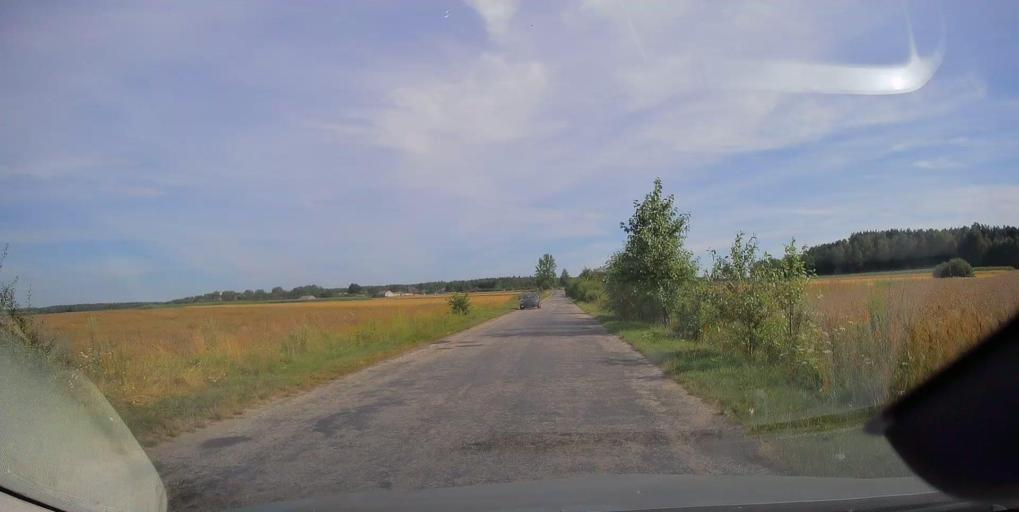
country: PL
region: Lodz Voivodeship
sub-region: Powiat opoczynski
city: Mniszkow
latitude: 51.4153
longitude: 20.0326
